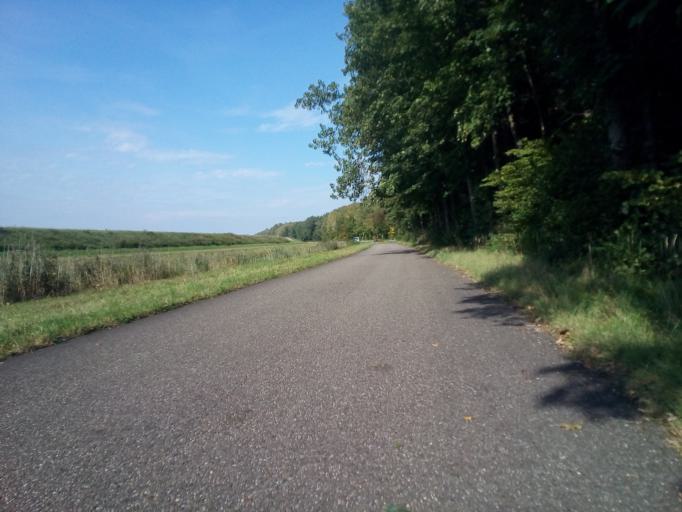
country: DE
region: Baden-Wuerttemberg
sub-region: Karlsruhe Region
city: Lichtenau
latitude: 48.7260
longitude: 7.9695
